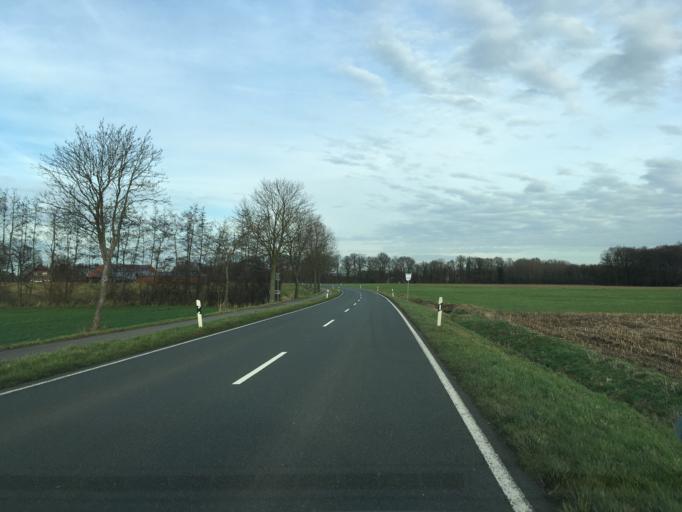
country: DE
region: North Rhine-Westphalia
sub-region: Regierungsbezirk Munster
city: Gescher
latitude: 51.9938
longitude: 7.0354
